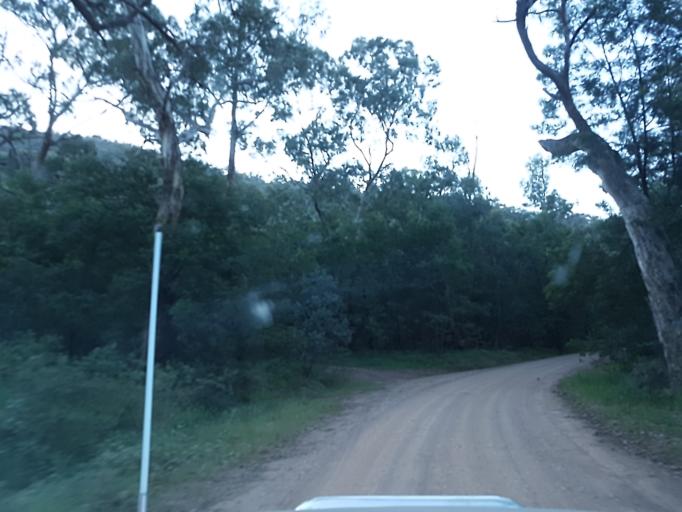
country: AU
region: Victoria
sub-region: Wellington
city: Heyfield
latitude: -37.4112
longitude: 147.0871
